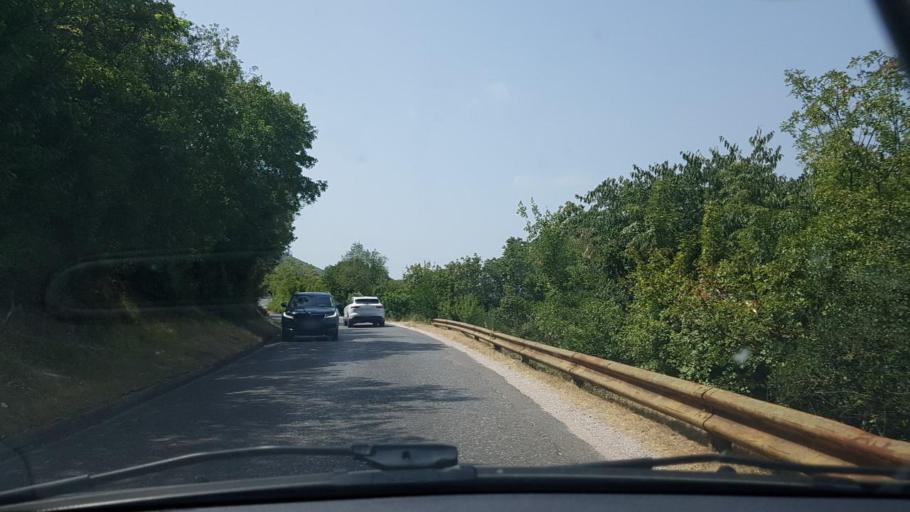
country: BA
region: Federation of Bosnia and Herzegovina
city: Tasovcici
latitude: 43.0355
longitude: 17.7246
